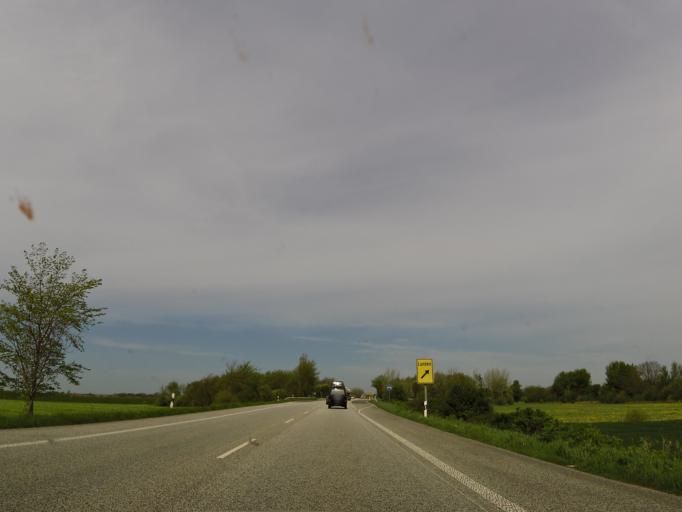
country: DE
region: Schleswig-Holstein
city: Tonning
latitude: 54.3055
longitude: 8.9610
